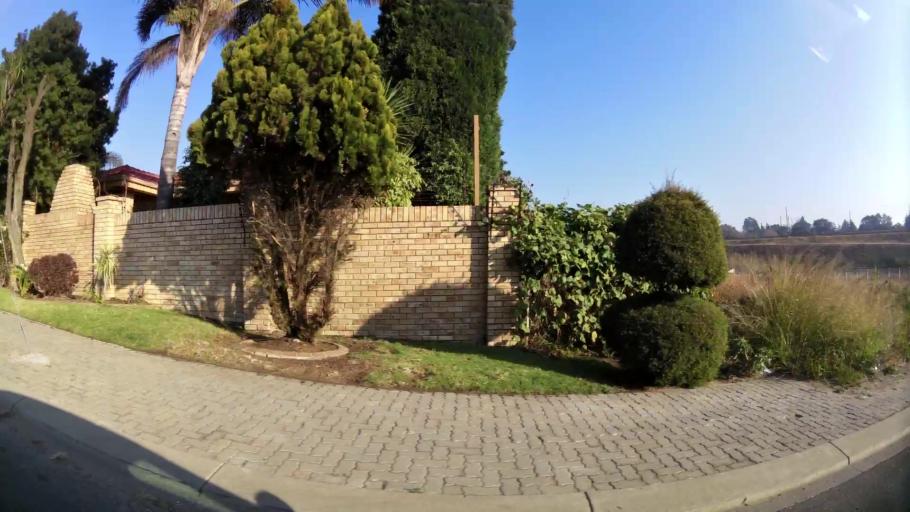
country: ZA
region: Gauteng
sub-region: City of Johannesburg Metropolitan Municipality
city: Modderfontein
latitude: -26.0864
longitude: 28.1040
